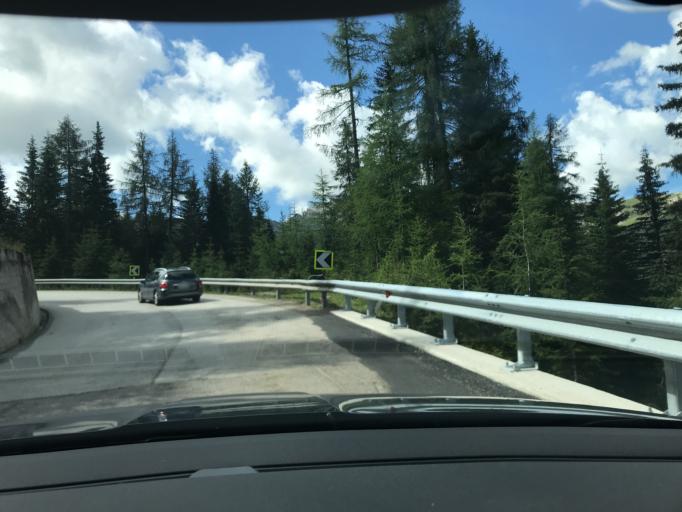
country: IT
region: Veneto
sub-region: Provincia di Belluno
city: Livinallongo del Col di Lana
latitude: 46.5439
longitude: 11.9731
